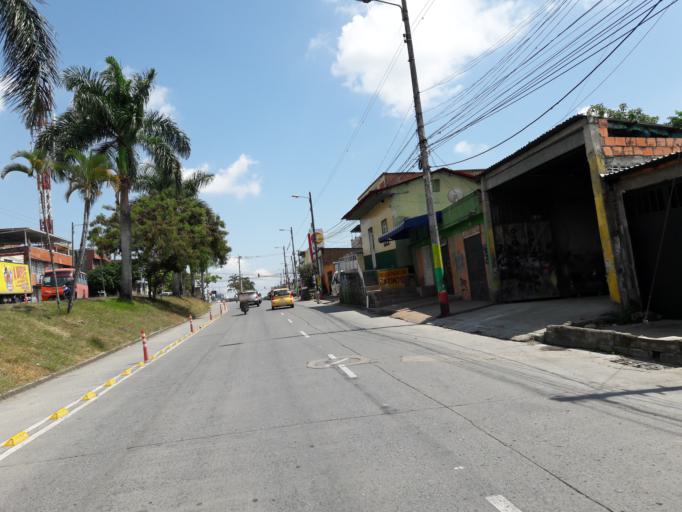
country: CO
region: Tolima
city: Ibague
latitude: 4.4368
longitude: -75.2302
